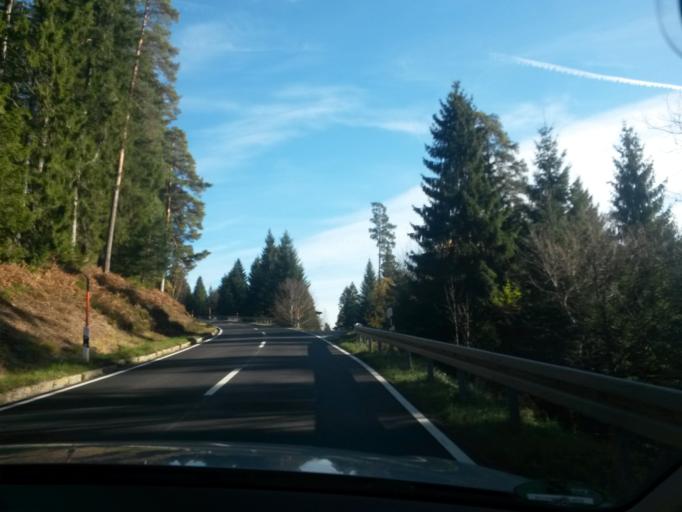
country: DE
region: Baden-Wuerttemberg
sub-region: Karlsruhe Region
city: Bad Rippoldsau-Schapbach
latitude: 48.4509
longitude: 8.2935
